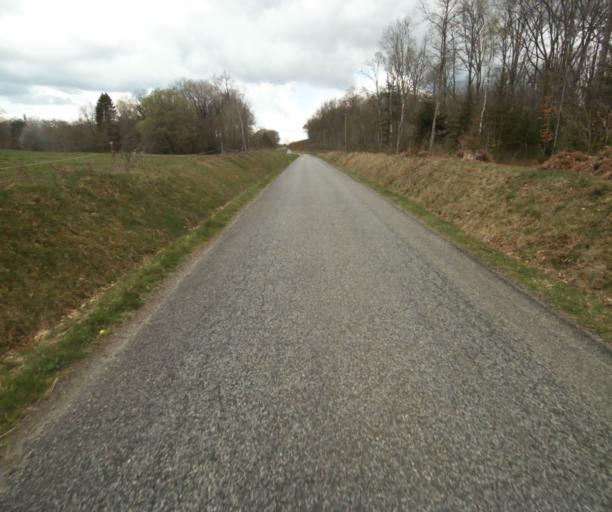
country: FR
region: Limousin
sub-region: Departement de la Correze
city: Correze
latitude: 45.2637
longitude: 1.9049
